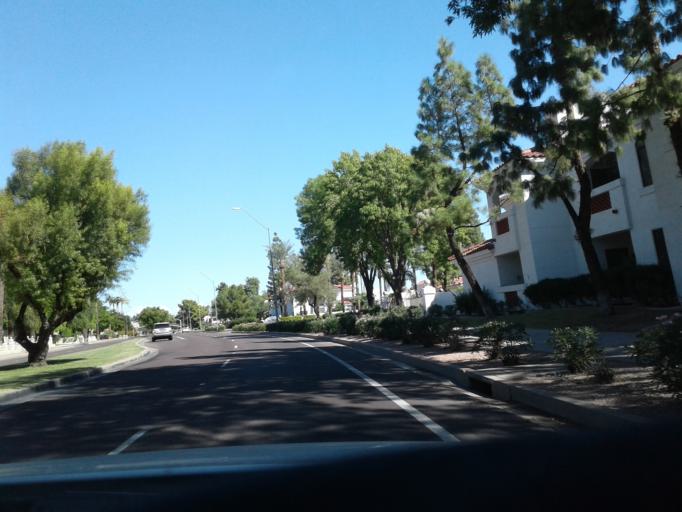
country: US
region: Arizona
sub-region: Maricopa County
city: Paradise Valley
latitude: 33.5546
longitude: -111.9042
